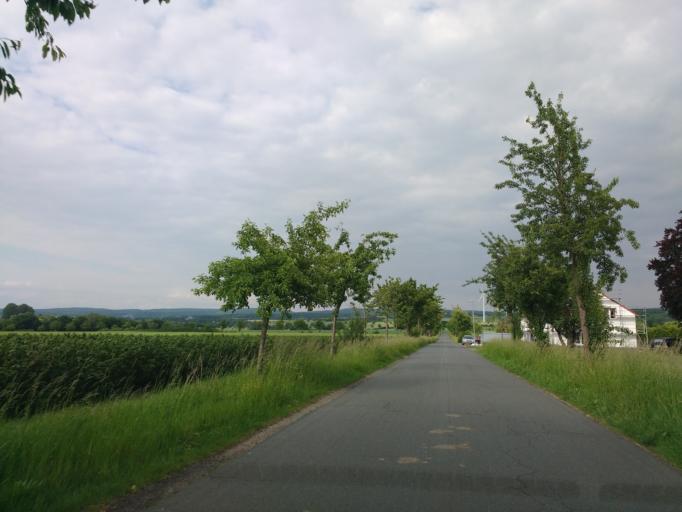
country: DE
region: North Rhine-Westphalia
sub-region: Regierungsbezirk Detmold
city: Schlangen
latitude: 51.7890
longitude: 8.8418
